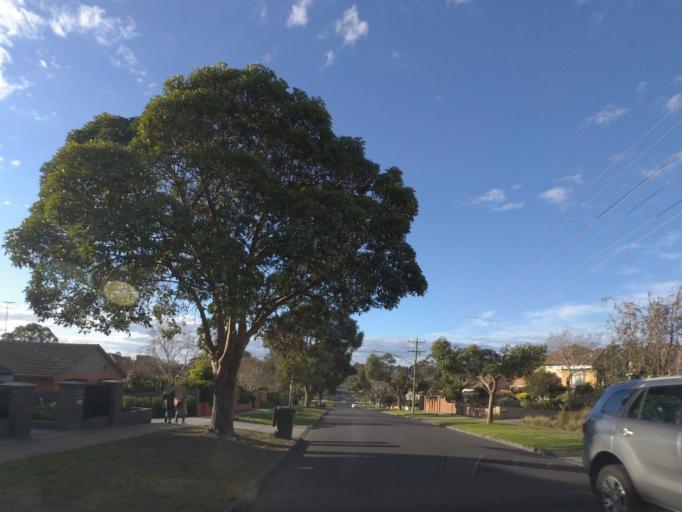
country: AU
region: Victoria
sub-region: Boroondara
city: Balwyn North
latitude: -37.7920
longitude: 145.0853
